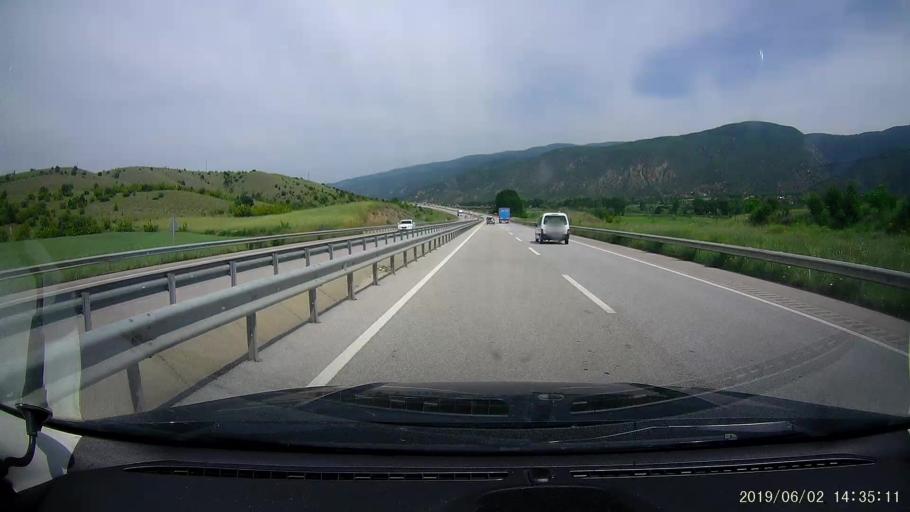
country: TR
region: Kastamonu
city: Tosya
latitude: 41.0403
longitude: 34.2087
